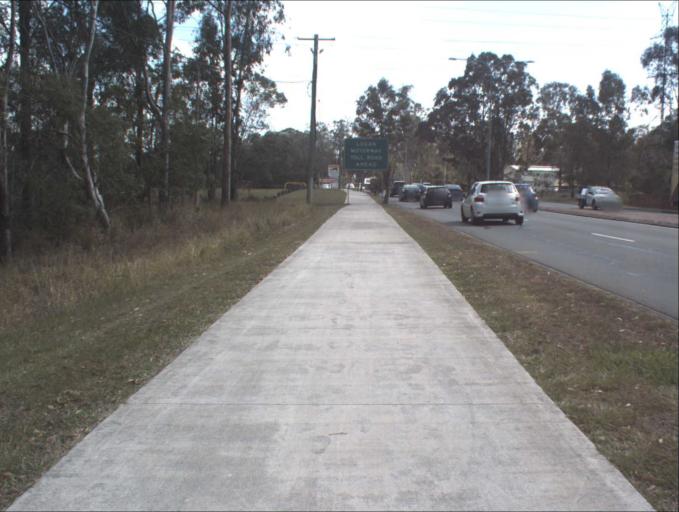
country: AU
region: Queensland
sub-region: Logan
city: Slacks Creek
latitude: -27.6582
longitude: 153.1424
